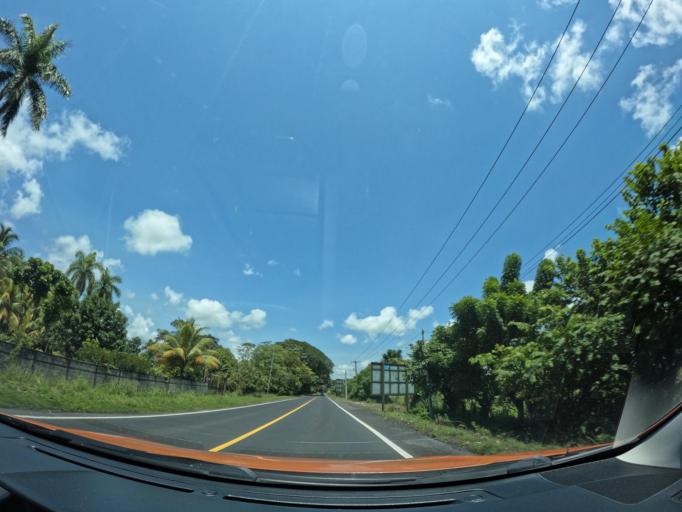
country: GT
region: Escuintla
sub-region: Municipio de Masagua
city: Masagua
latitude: 14.1845
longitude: -90.8622
